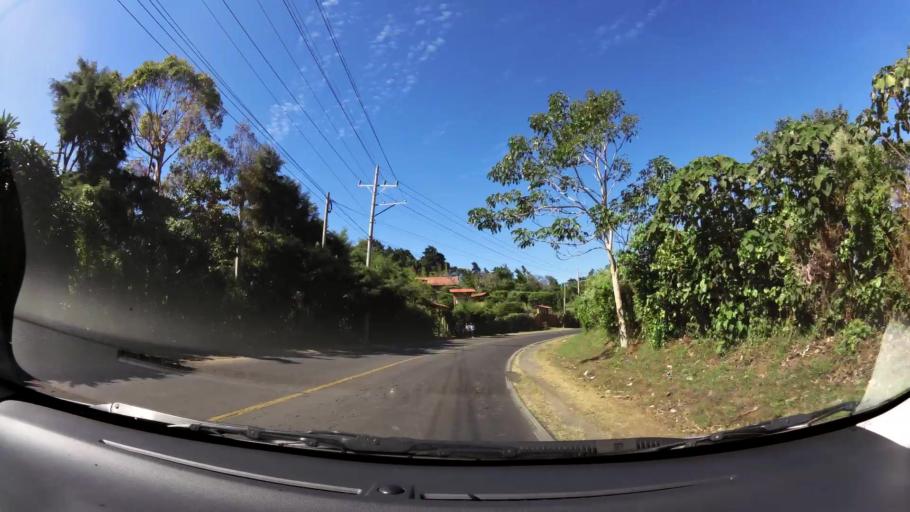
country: SV
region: Ahuachapan
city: Concepcion de Ataco
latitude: 13.8477
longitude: -89.8380
